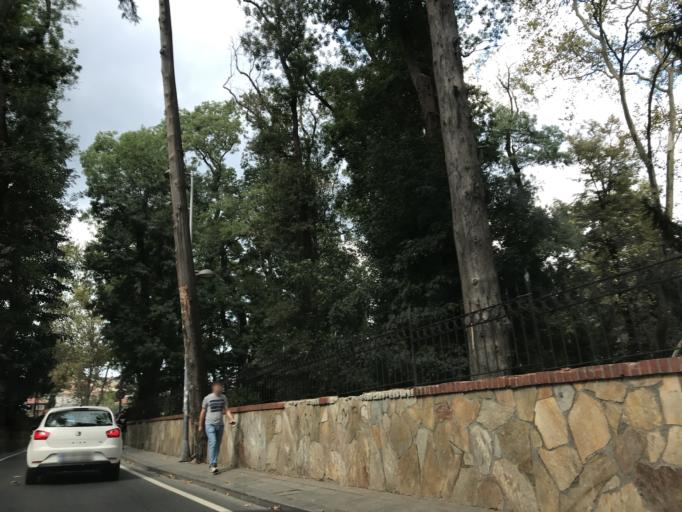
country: TR
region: Istanbul
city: Arikoey
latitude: 41.1714
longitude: 29.0535
